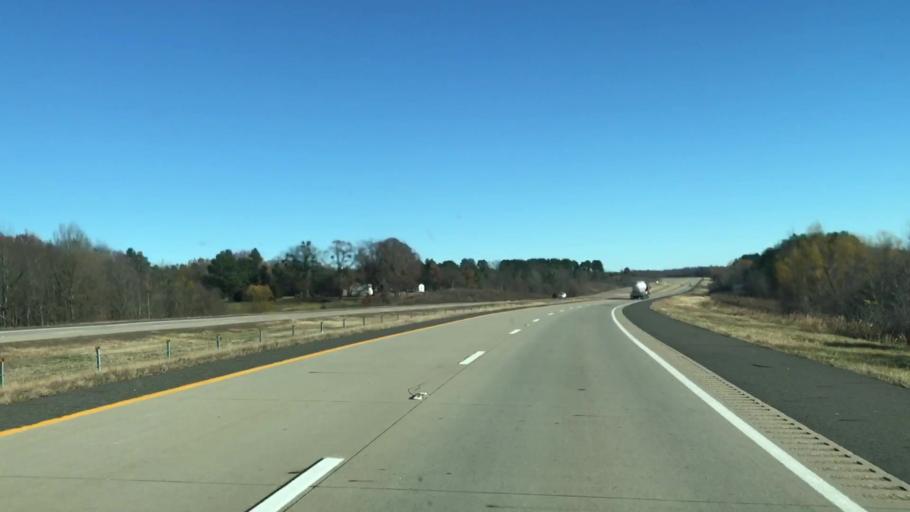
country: US
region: Texas
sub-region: Cass County
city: Queen City
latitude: 33.1570
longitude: -93.8883
